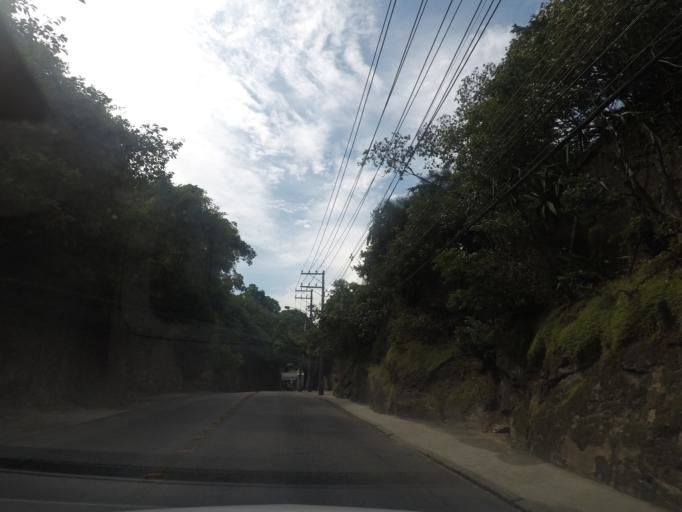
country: BR
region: Rio de Janeiro
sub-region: Rio De Janeiro
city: Rio de Janeiro
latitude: -22.8127
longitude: -43.1758
